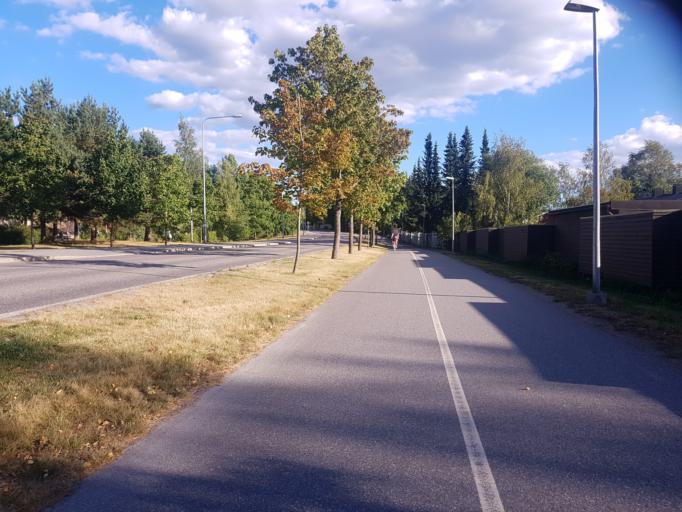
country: FI
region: Uusimaa
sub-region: Helsinki
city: Vantaa
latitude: 60.2633
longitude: 24.9840
